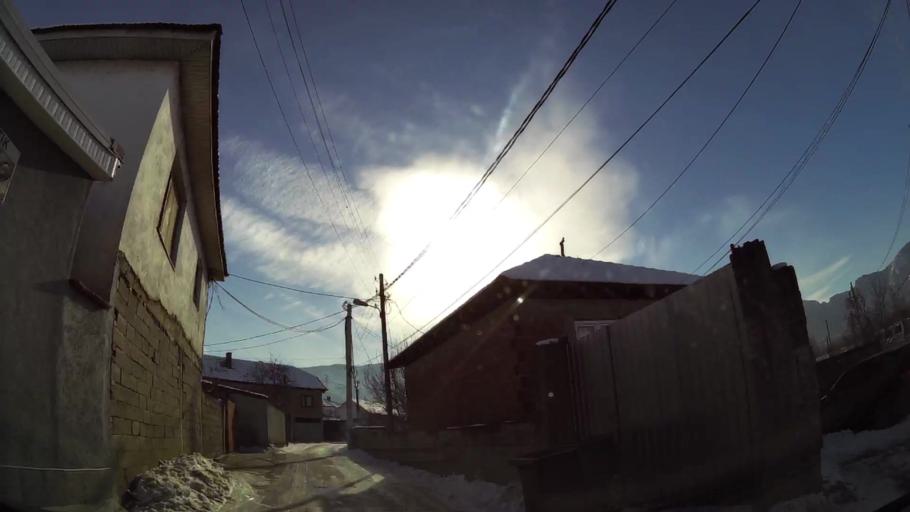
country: MK
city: Grchec
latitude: 41.9912
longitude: 21.3256
